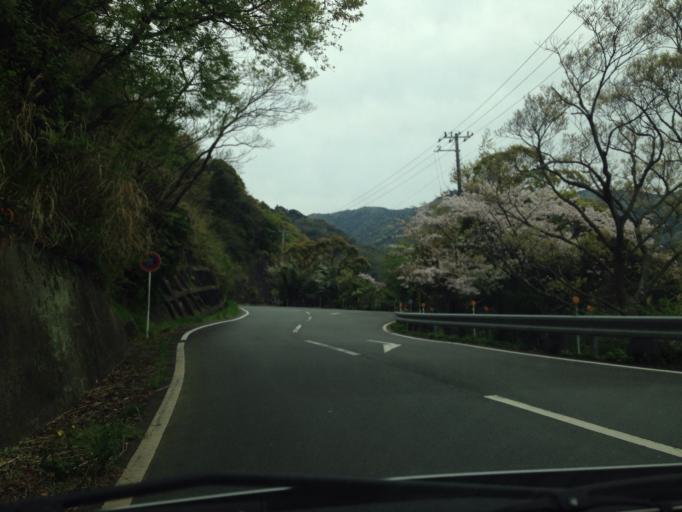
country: JP
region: Shizuoka
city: Heda
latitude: 35.0225
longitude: 138.8138
